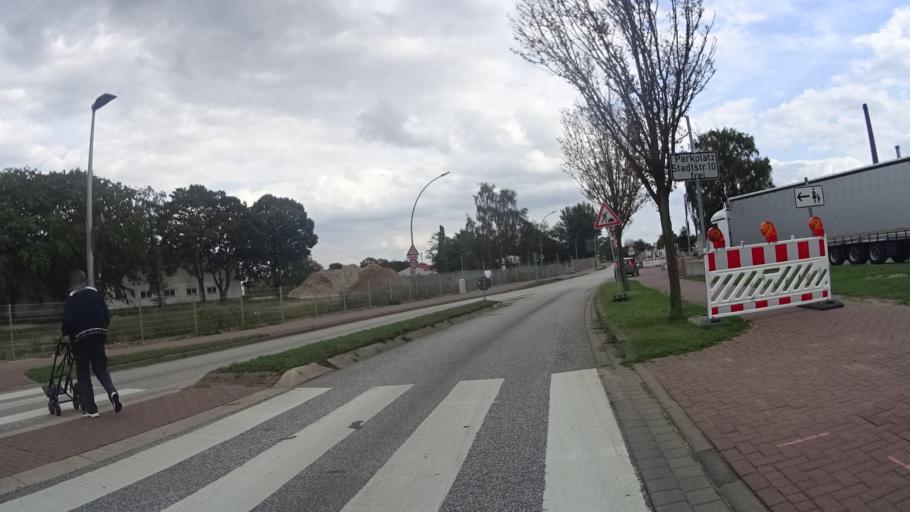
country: DE
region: Schleswig-Holstein
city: Gluckstadt
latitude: 53.7856
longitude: 9.4262
